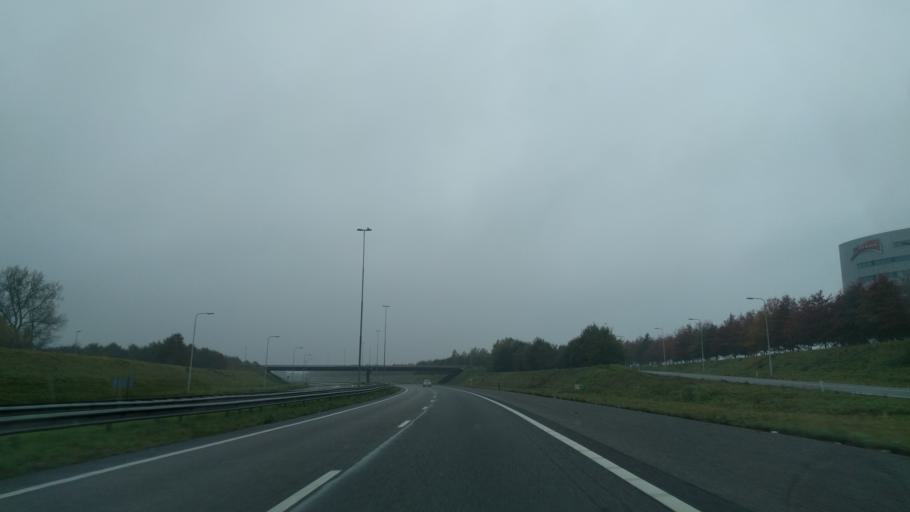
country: NL
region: North Brabant
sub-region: Gemeente Zundert
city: Zundert
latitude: 51.5702
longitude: 4.6650
